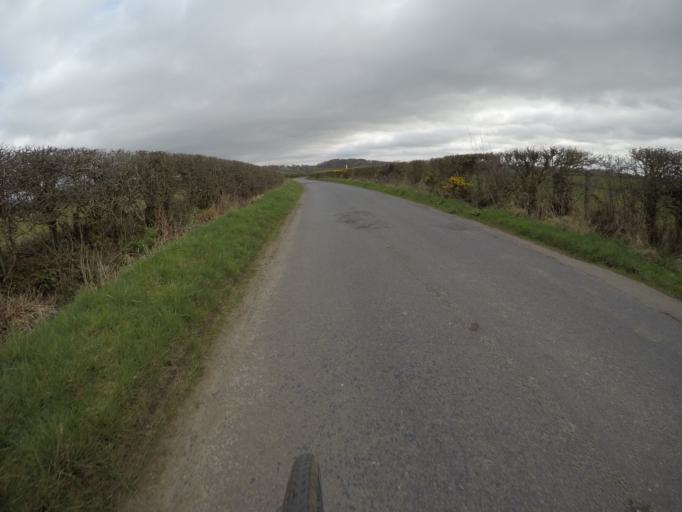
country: GB
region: Scotland
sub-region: East Ayrshire
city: Stewarton
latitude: 55.6720
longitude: -4.5626
